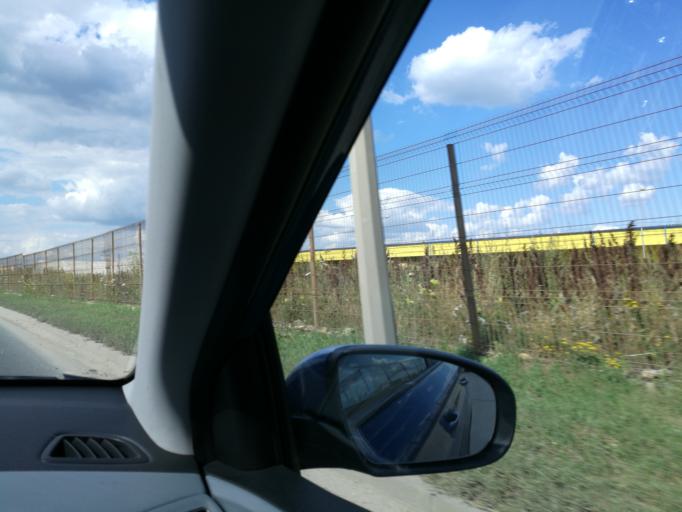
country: RO
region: Ilfov
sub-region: Comuna Glina
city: Catelu
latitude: 44.4083
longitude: 26.2185
